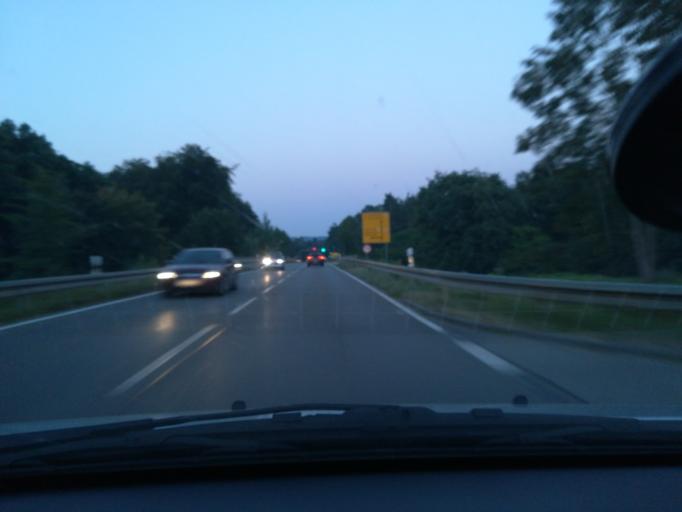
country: DE
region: Baden-Wuerttemberg
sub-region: Freiburg Region
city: Rielasingen-Worblingen
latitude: 47.7459
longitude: 8.8136
